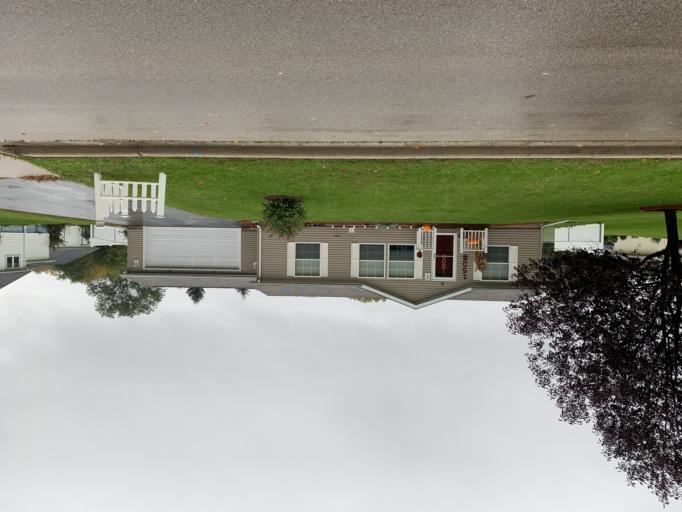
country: US
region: Wisconsin
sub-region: Oconto County
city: Oconto
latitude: 44.8986
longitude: -87.8646
